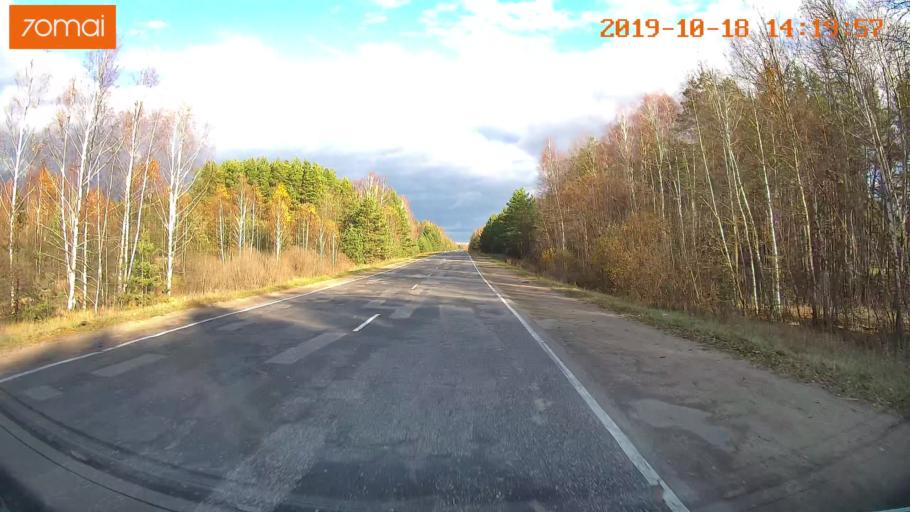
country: RU
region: Rjazan
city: Tuma
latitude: 55.1426
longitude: 40.4205
